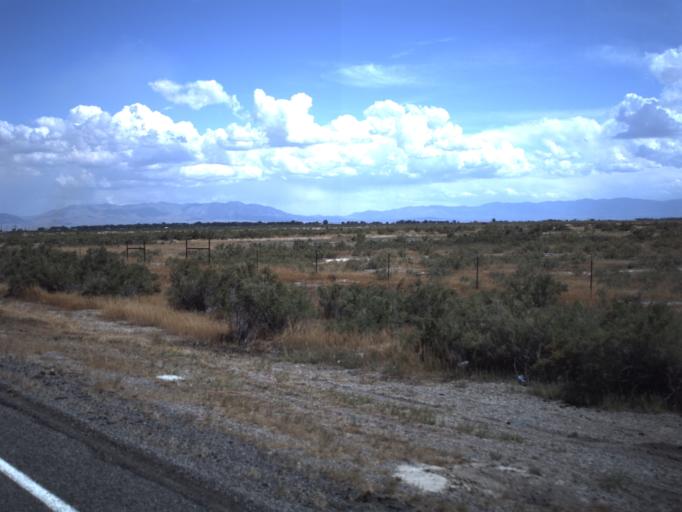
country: US
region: Utah
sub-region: Millard County
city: Delta
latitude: 39.3298
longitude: -112.7217
